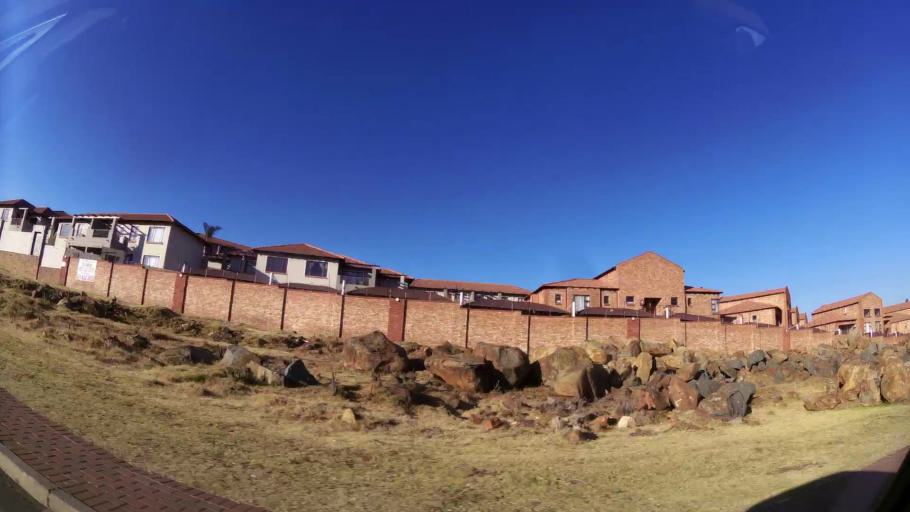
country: ZA
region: Gauteng
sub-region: City of Johannesburg Metropolitan Municipality
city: Johannesburg
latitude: -26.2912
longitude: 28.0724
